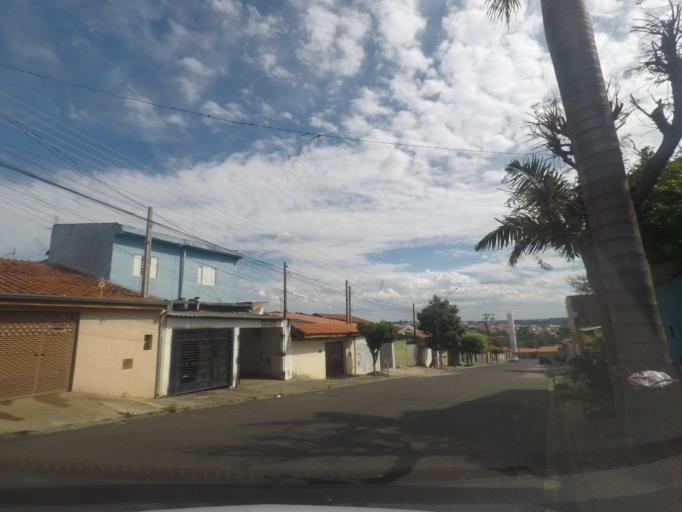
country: BR
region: Sao Paulo
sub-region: Sumare
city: Sumare
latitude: -22.8058
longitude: -47.2725
